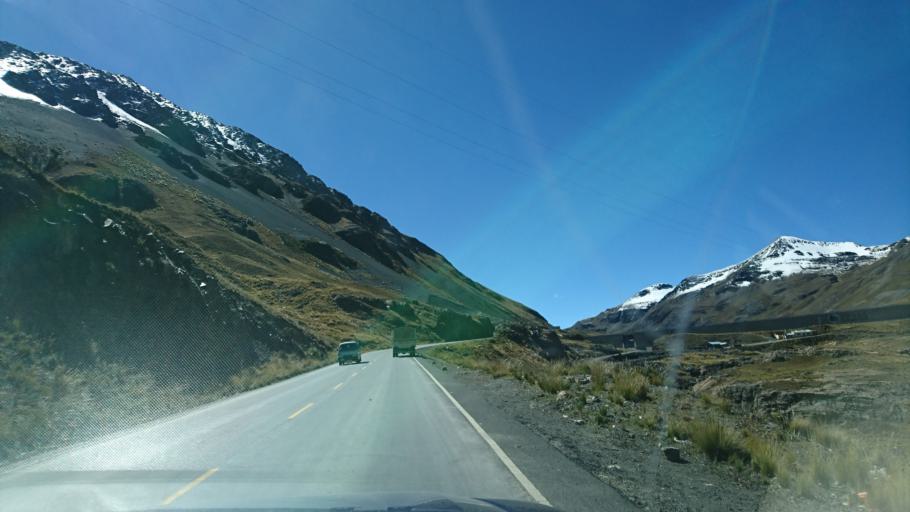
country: BO
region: La Paz
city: La Paz
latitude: -16.4098
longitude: -68.0507
